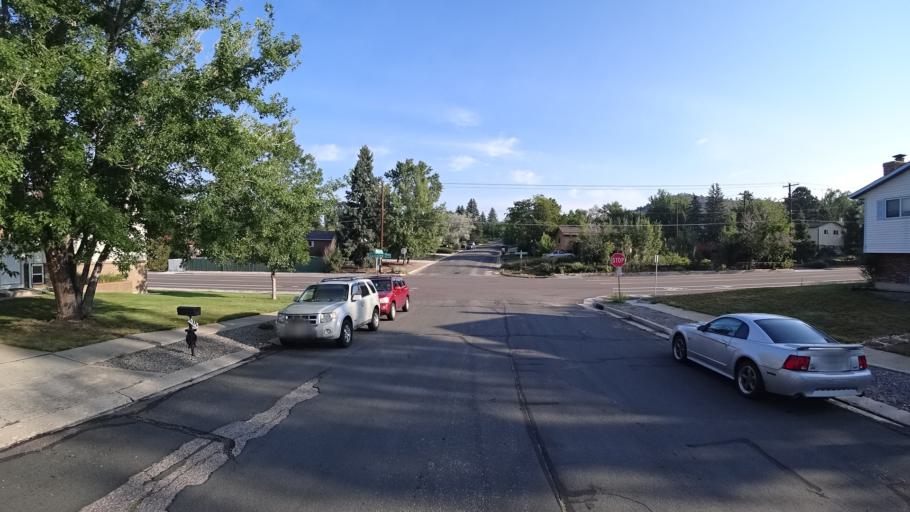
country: US
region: Colorado
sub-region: El Paso County
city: Colorado Springs
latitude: 38.8893
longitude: -104.8075
